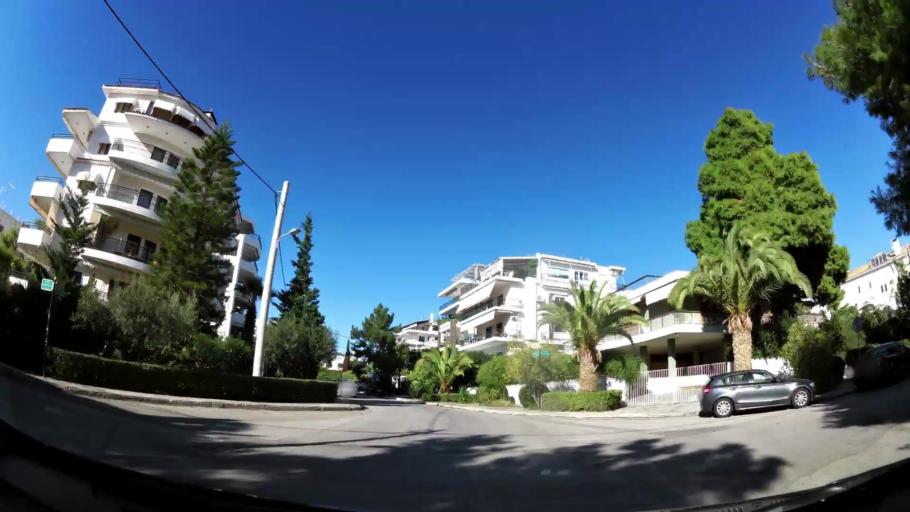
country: GR
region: Attica
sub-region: Nomarchia Anatolikis Attikis
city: Voula
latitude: 37.8460
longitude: 23.7668
